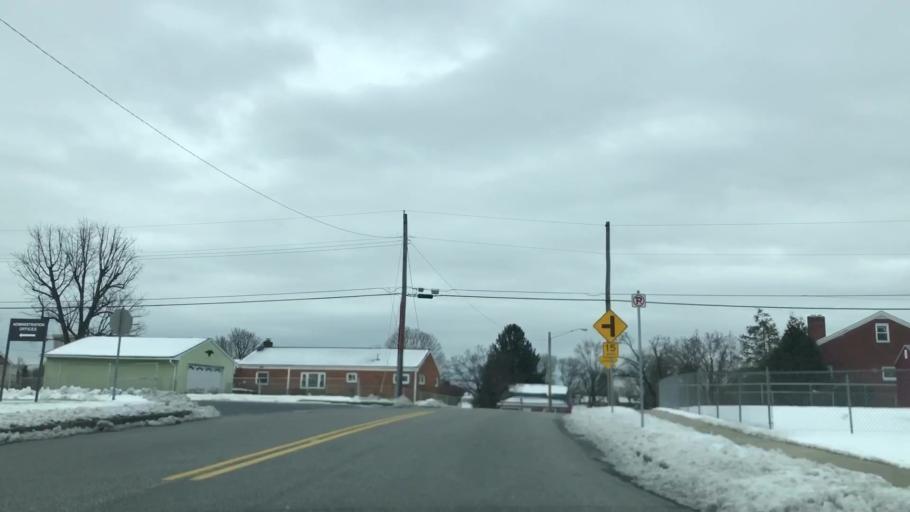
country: US
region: Pennsylvania
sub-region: Dauphin County
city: Colonial Park
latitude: 40.2977
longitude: -76.8064
